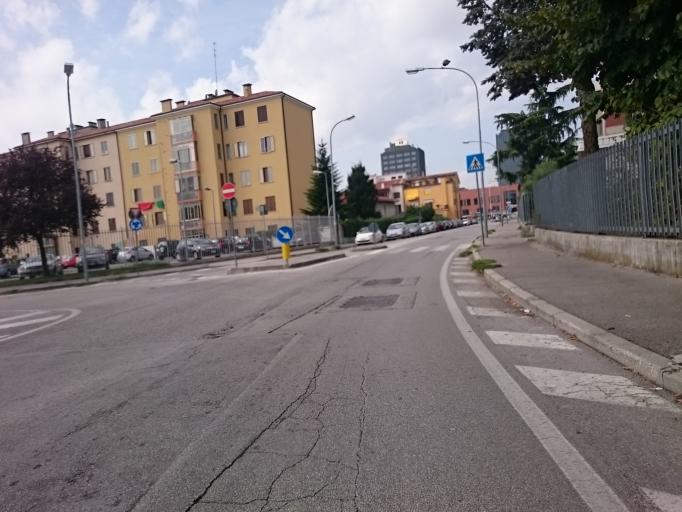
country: IT
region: Veneto
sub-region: Provincia di Padova
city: Padova
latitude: 45.4107
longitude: 11.9043
